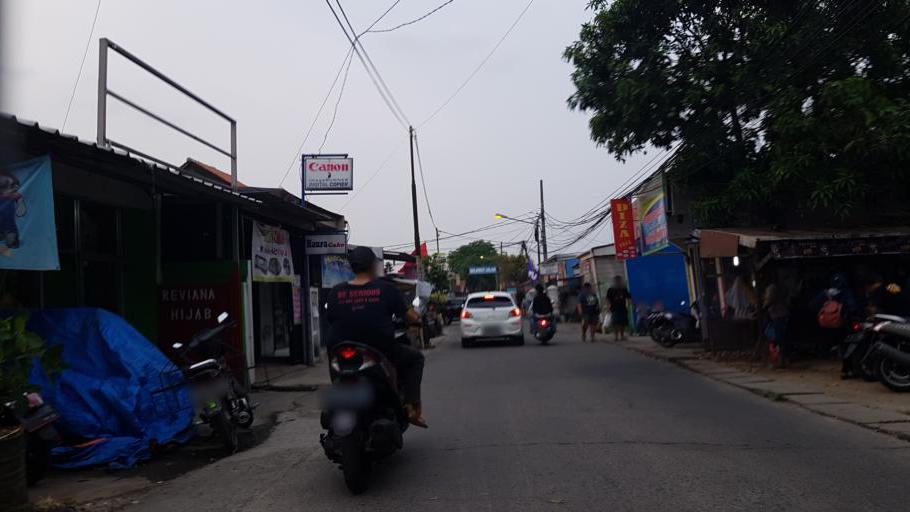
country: ID
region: West Java
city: Depok
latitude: -6.3757
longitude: 106.8013
